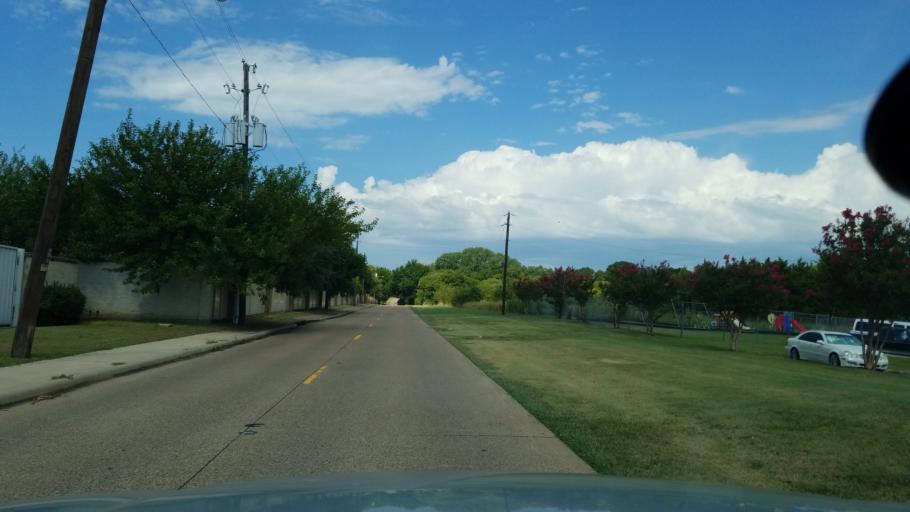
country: US
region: Texas
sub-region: Dallas County
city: Duncanville
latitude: 32.6549
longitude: -96.8579
